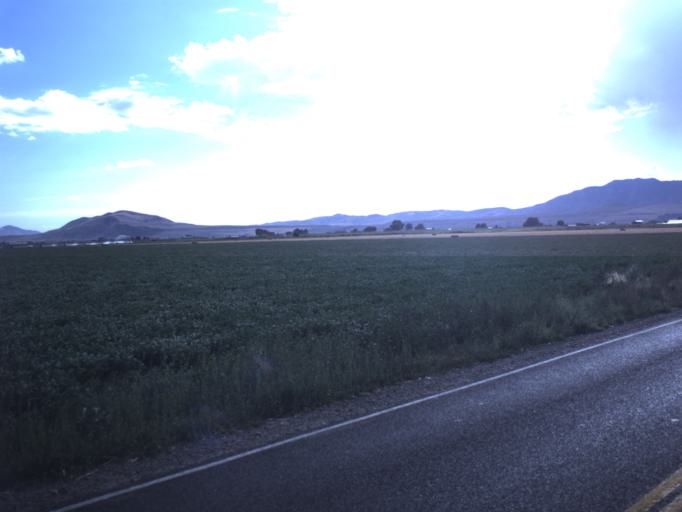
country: US
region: Utah
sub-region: Cache County
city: Lewiston
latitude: 41.9757
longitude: -111.8781
